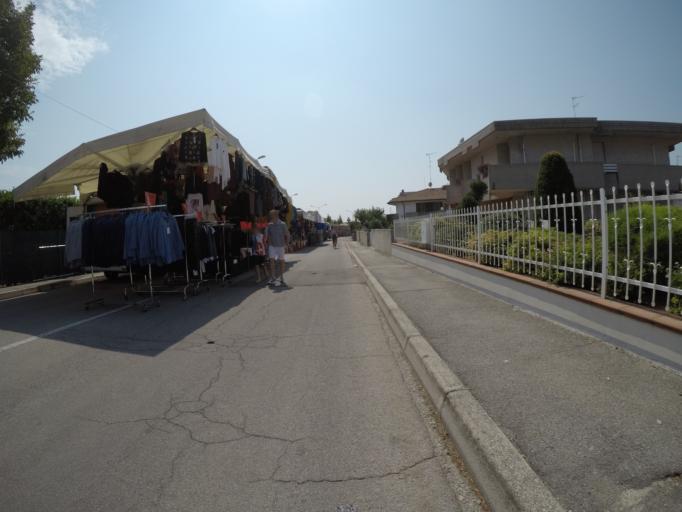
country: IT
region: Veneto
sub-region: Provincia di Rovigo
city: Lendinara
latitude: 45.0817
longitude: 11.6033
